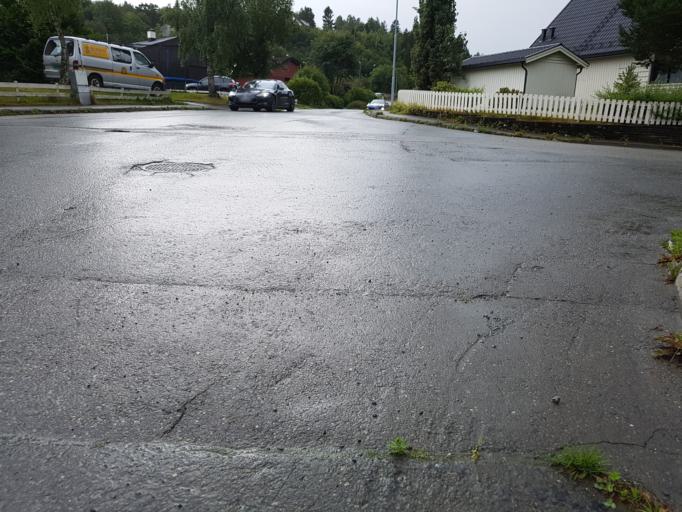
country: NO
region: Sor-Trondelag
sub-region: Trondheim
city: Trondheim
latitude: 63.4121
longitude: 10.4867
